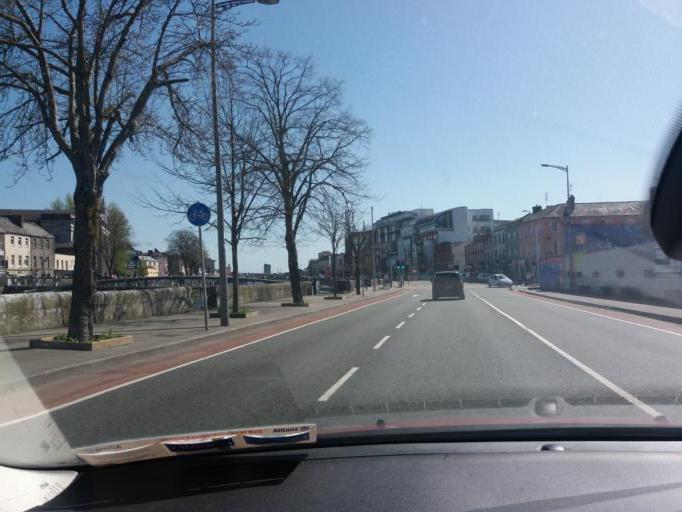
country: IE
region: Munster
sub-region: County Cork
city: Cork
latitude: 51.9010
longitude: -8.4772
